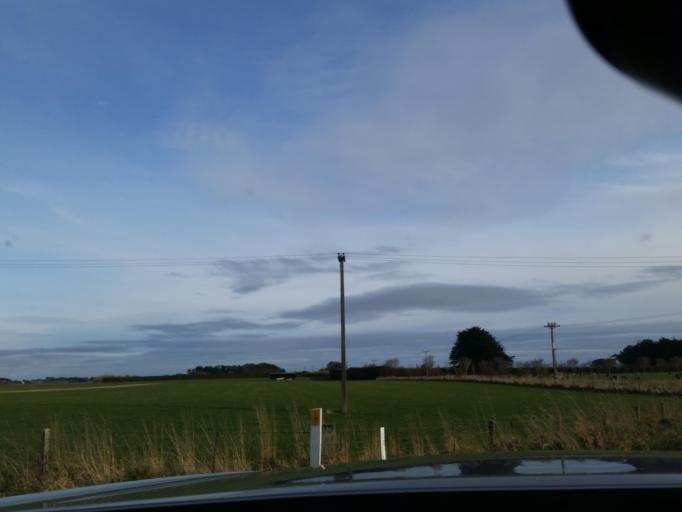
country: NZ
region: Southland
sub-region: Invercargill City
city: Invercargill
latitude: -46.2986
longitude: 168.3040
